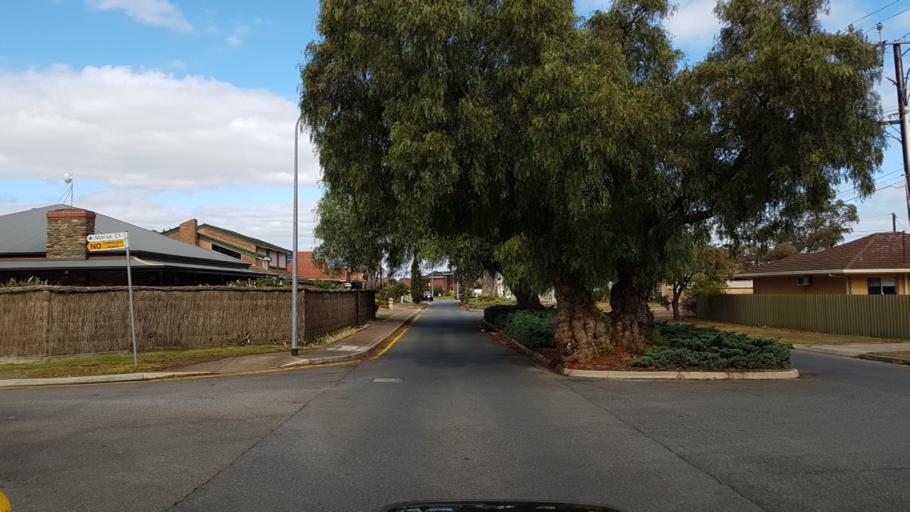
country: AU
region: South Australia
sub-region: Charles Sturt
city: Seaton
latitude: -34.9066
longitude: 138.5176
